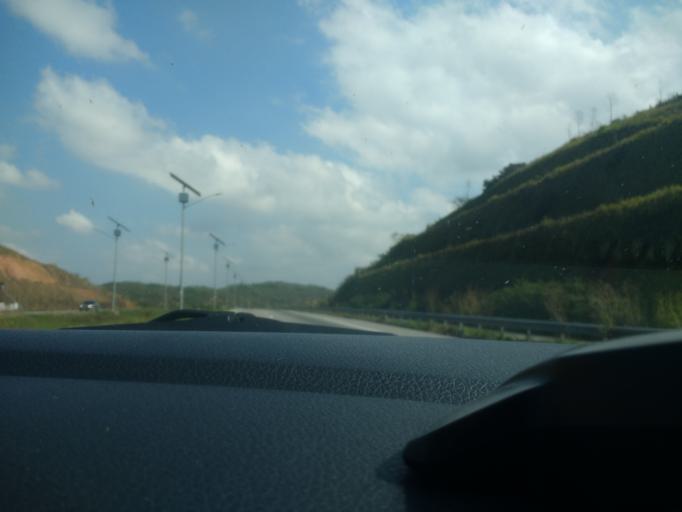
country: BR
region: Rio de Janeiro
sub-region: Queimados
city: Queimados
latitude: -22.6875
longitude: -43.5143
